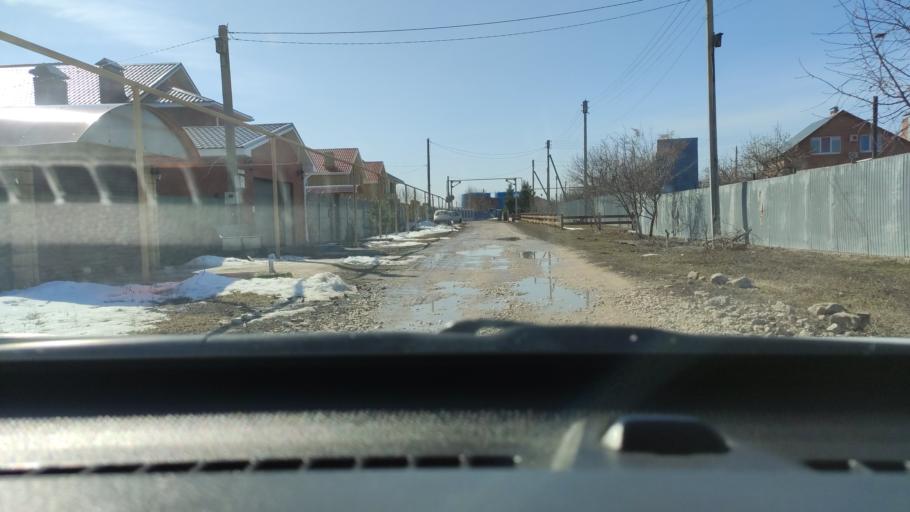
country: RU
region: Samara
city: Podstepki
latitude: 53.5105
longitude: 49.1860
